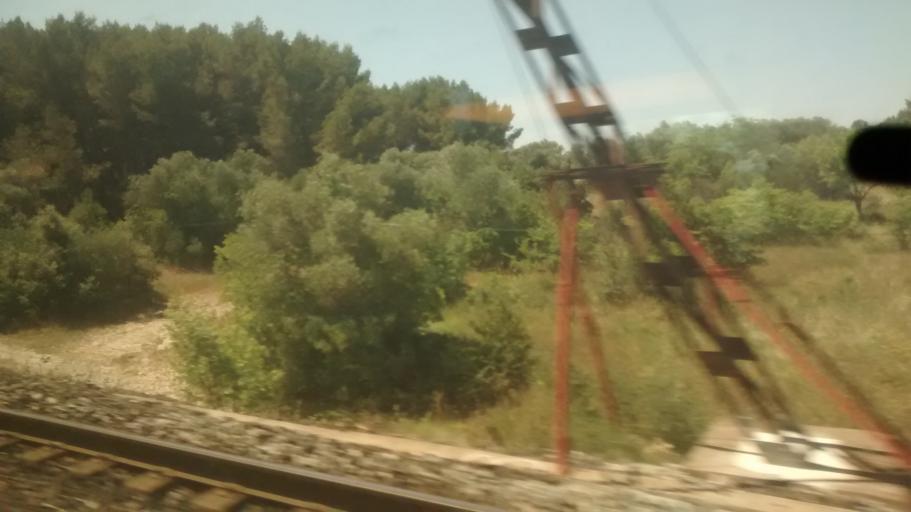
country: FR
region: Languedoc-Roussillon
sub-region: Departement du Gard
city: Vestric-et-Candiac
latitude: 43.7494
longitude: 4.2549
